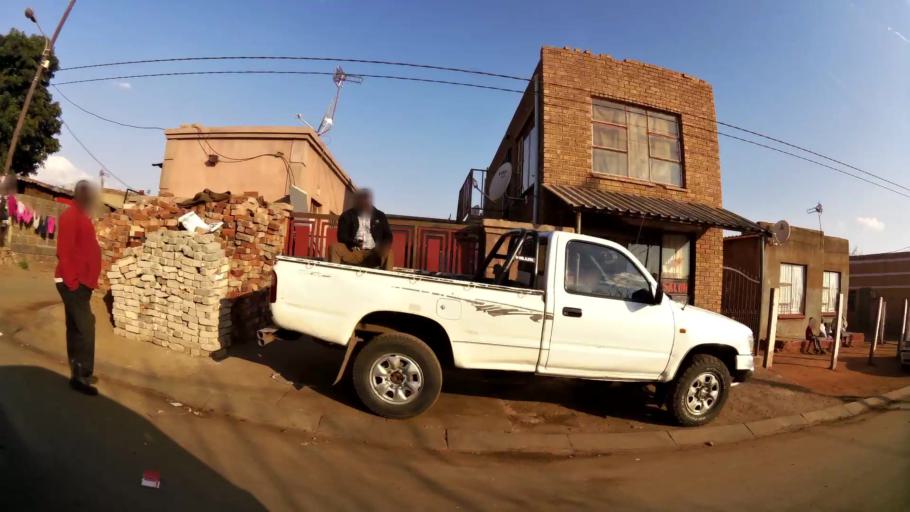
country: ZA
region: Gauteng
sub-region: Ekurhuleni Metropolitan Municipality
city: Tembisa
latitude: -25.9669
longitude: 28.2122
